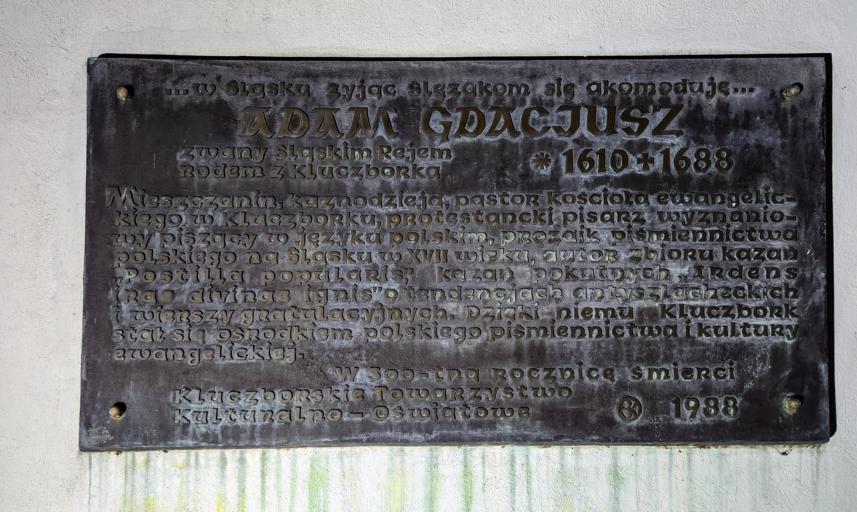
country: PL
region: Opole Voivodeship
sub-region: Powiat kluczborski
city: Kluczbork
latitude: 50.9729
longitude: 18.2129
